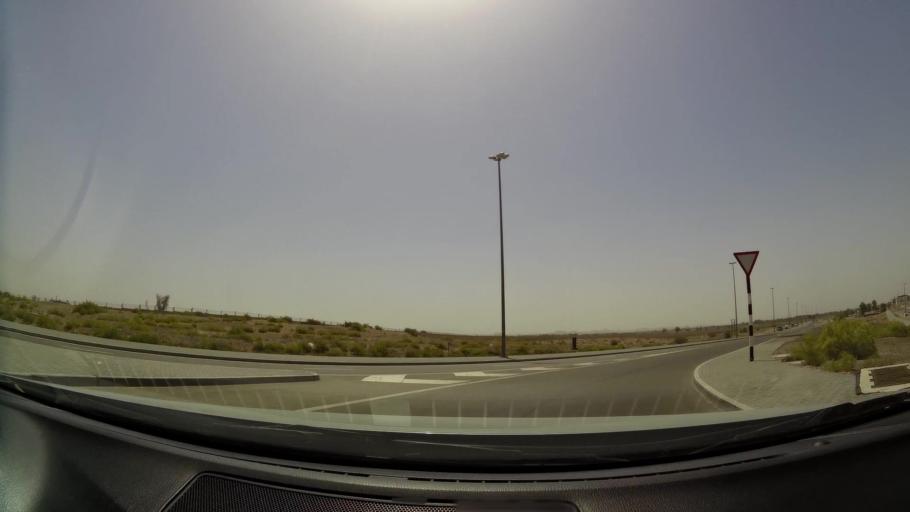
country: OM
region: Al Buraimi
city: Al Buraymi
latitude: 24.3127
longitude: 55.7568
